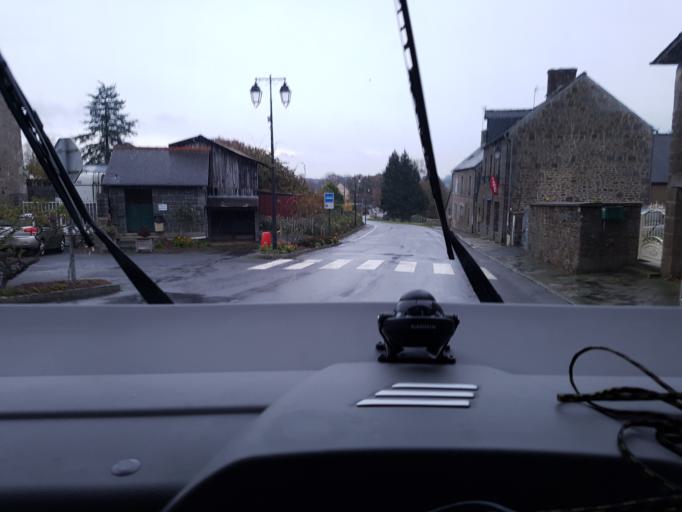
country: FR
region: Brittany
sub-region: Departement d'Ille-et-Vilaine
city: Saint-Marc-le-Blanc
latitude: 48.3590
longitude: -1.3804
